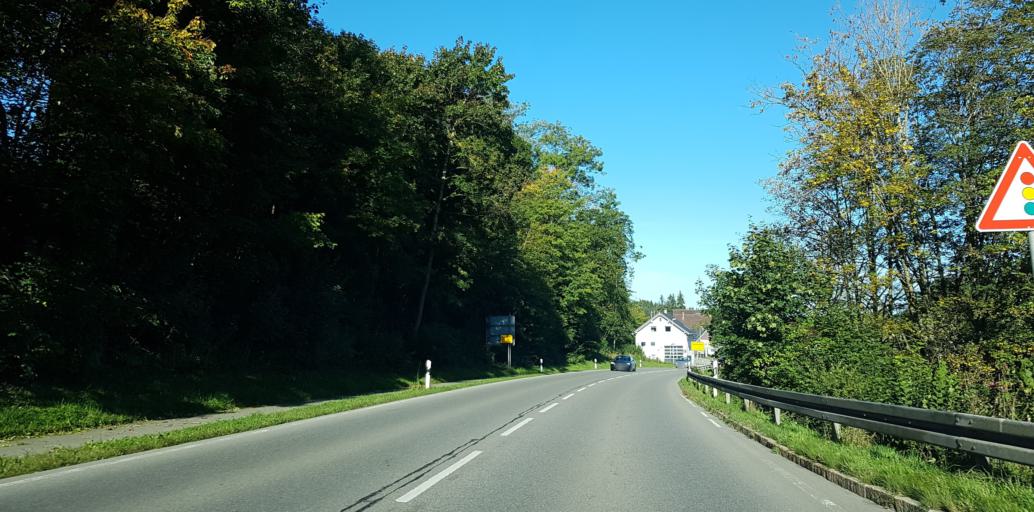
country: DE
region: Baden-Wuerttemberg
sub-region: Tuebingen Region
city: Leutkirch im Allgau
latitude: 47.8424
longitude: 9.9472
